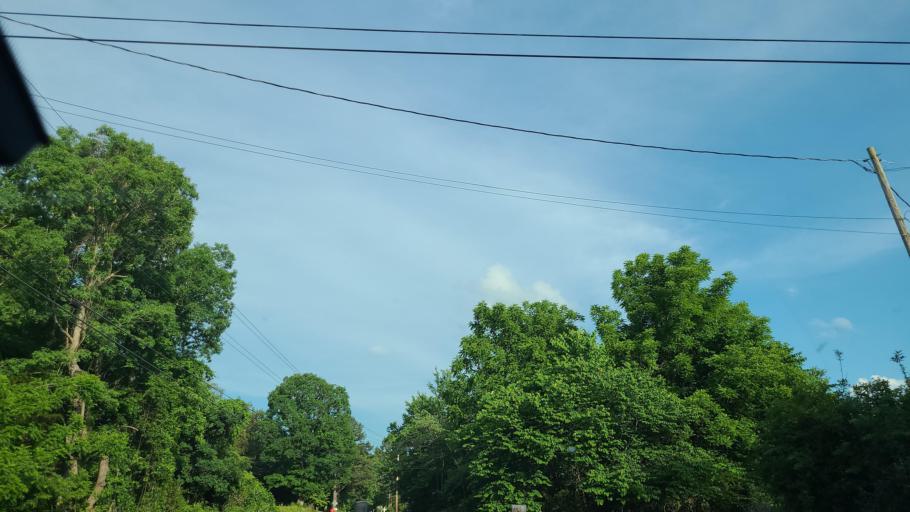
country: US
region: Kentucky
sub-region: Whitley County
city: Corbin
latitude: 36.8888
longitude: -84.2184
